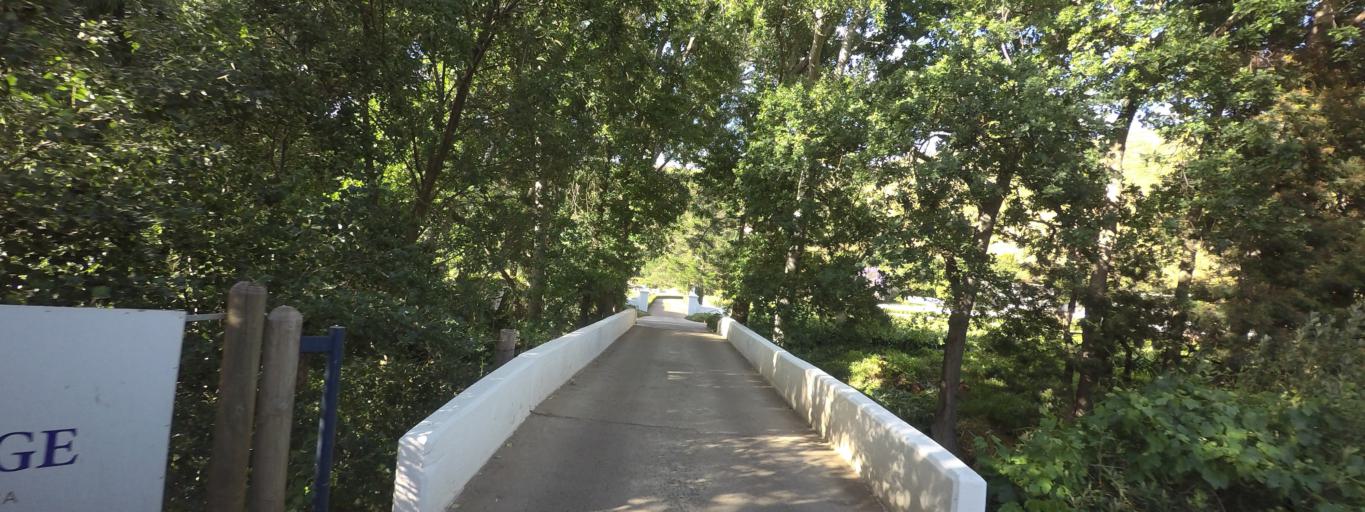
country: ZA
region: Western Cape
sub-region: Cape Winelands District Municipality
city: Paarl
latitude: -33.8989
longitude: 19.0933
